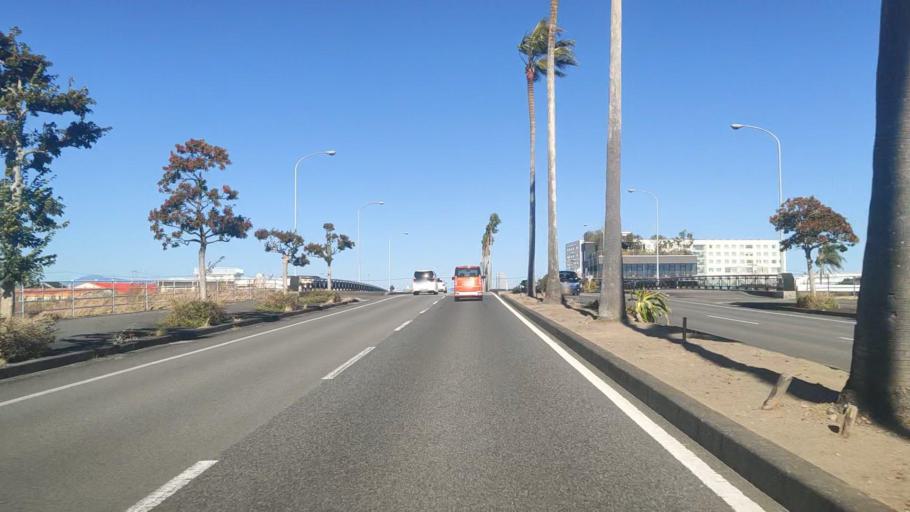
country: JP
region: Miyazaki
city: Miyazaki-shi
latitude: 31.9189
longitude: 131.4508
